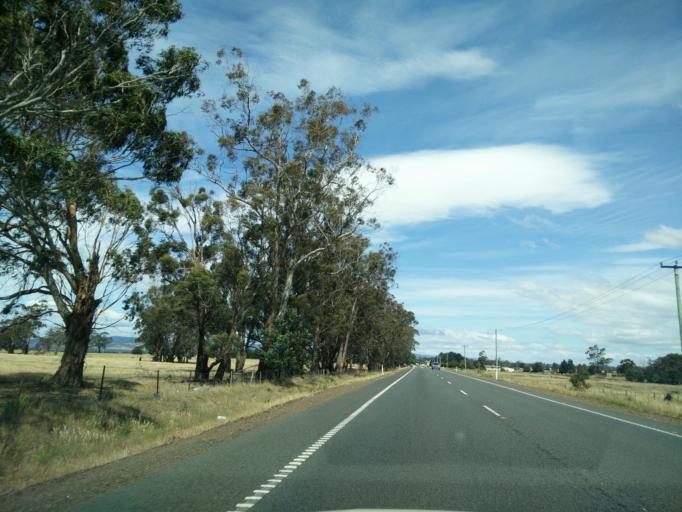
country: AU
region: Tasmania
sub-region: Northern Midlands
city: Evandale
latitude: -41.7980
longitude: 147.3958
